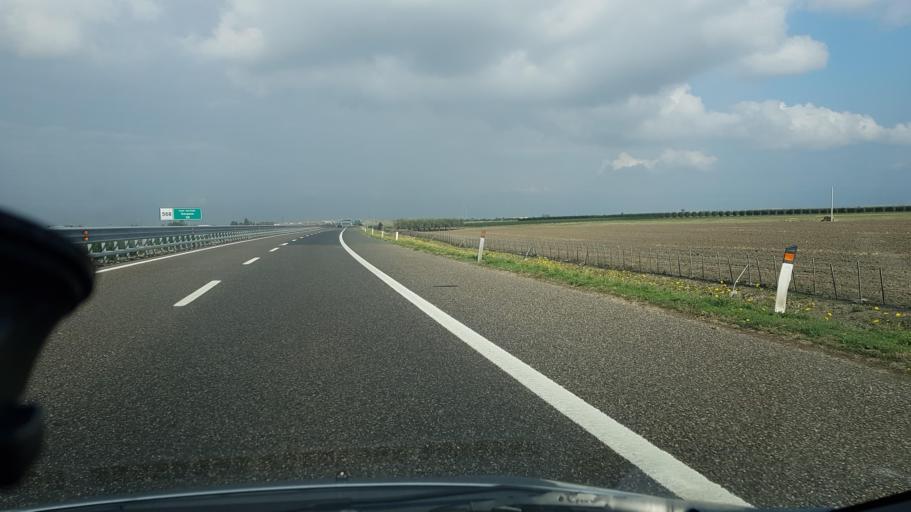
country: IT
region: Apulia
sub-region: Provincia di Foggia
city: Carapelle
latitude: 41.4045
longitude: 15.6726
